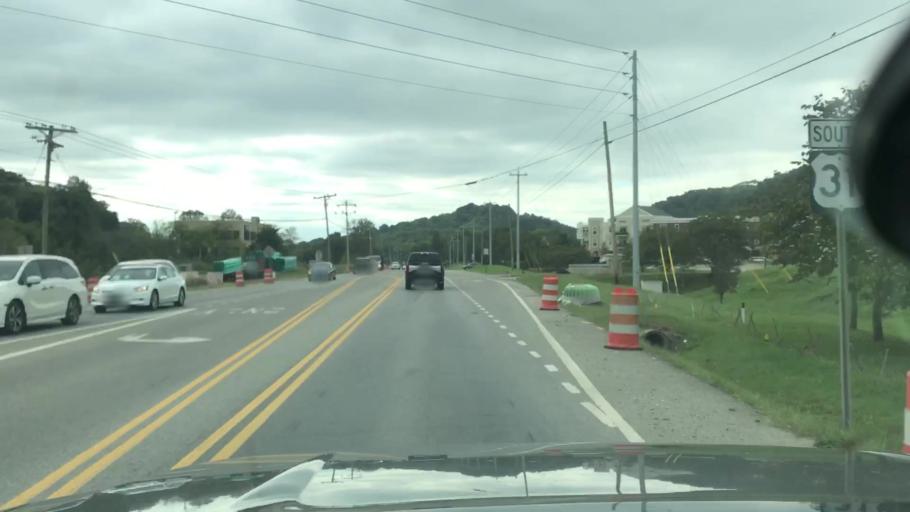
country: US
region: Tennessee
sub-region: Williamson County
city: Franklin
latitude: 35.9728
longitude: -86.8336
